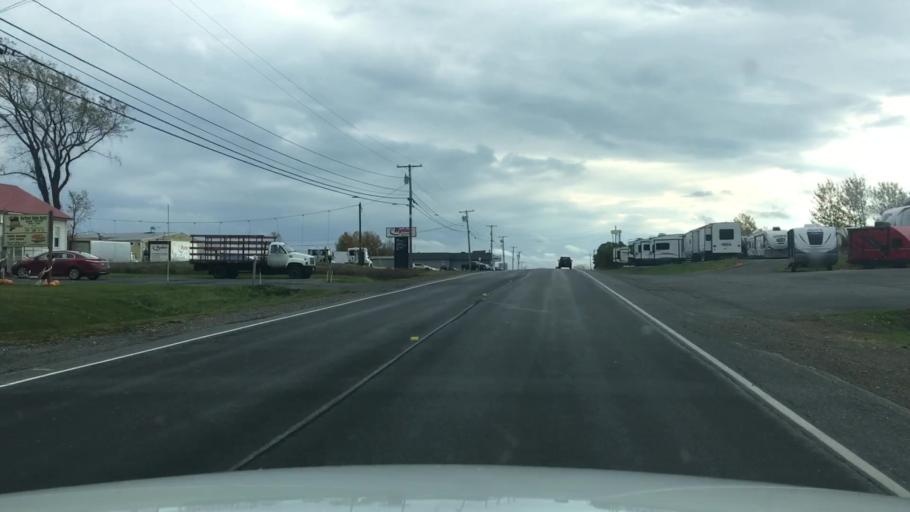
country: US
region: Maine
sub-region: Aroostook County
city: Presque Isle
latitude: 46.6605
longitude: -68.0081
